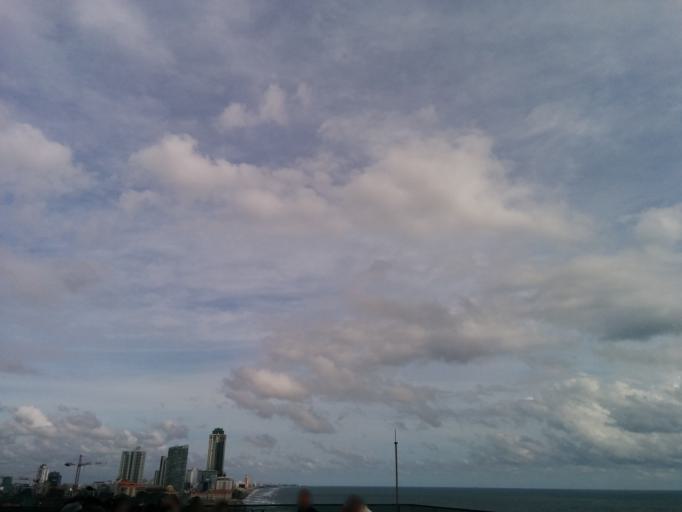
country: LK
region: Western
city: Colombo
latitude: 6.9330
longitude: 79.8417
